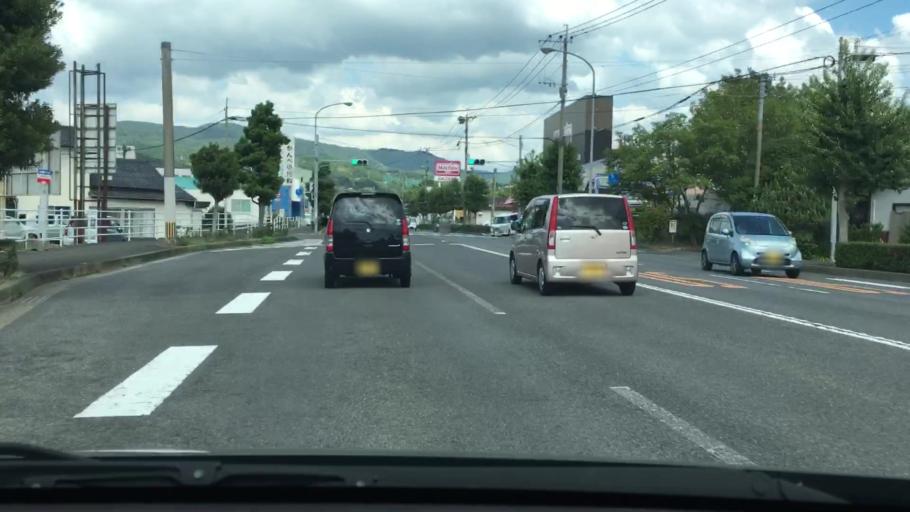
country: JP
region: Nagasaki
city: Sasebo
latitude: 33.2077
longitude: 129.6909
